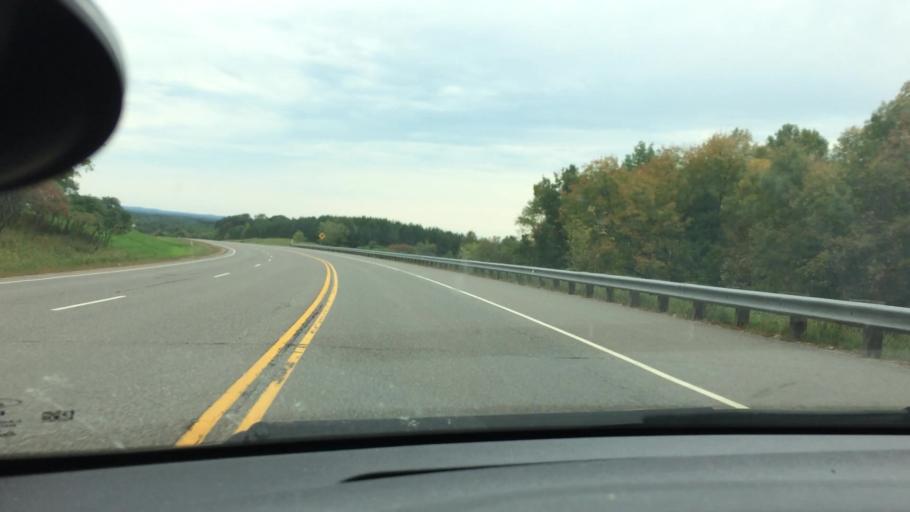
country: US
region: Wisconsin
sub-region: Clark County
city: Neillsville
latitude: 44.5660
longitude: -90.6634
